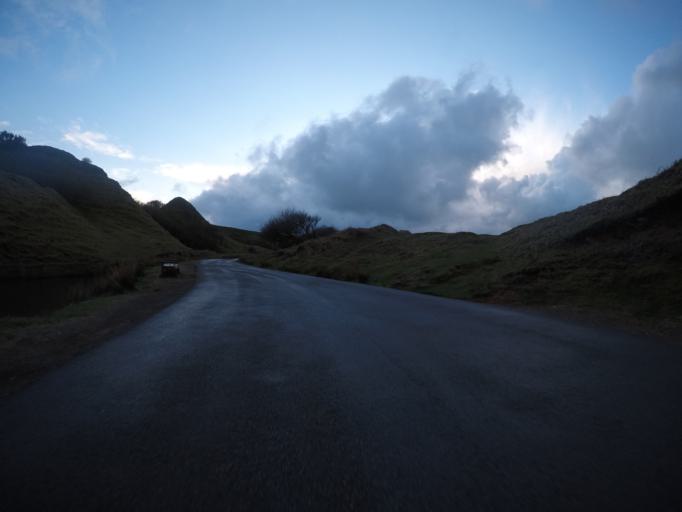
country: GB
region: Scotland
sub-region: Highland
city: Portree
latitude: 57.5839
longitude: -6.3270
